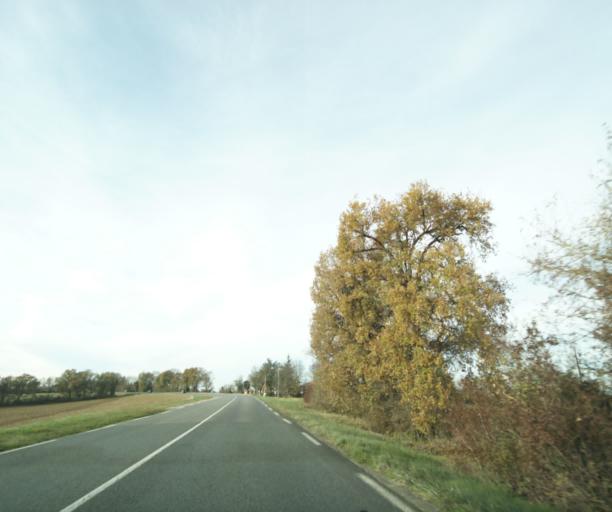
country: FR
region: Midi-Pyrenees
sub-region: Departement du Gers
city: Gimont
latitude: 43.6058
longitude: 0.9923
